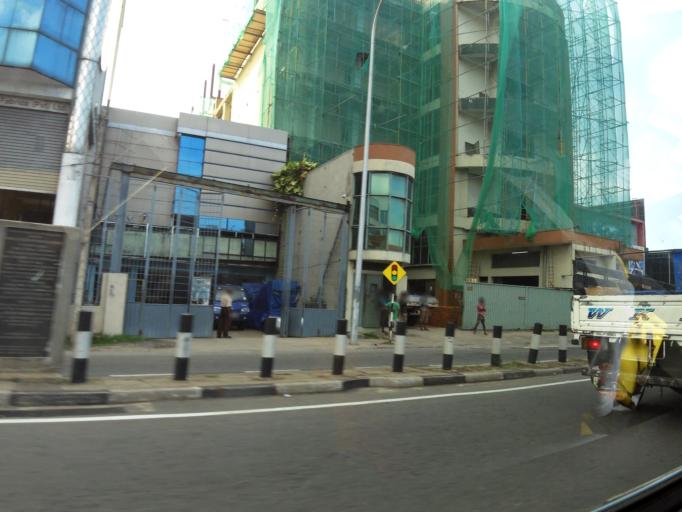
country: LK
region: Western
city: Kolonnawa
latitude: 6.9391
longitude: 79.8782
